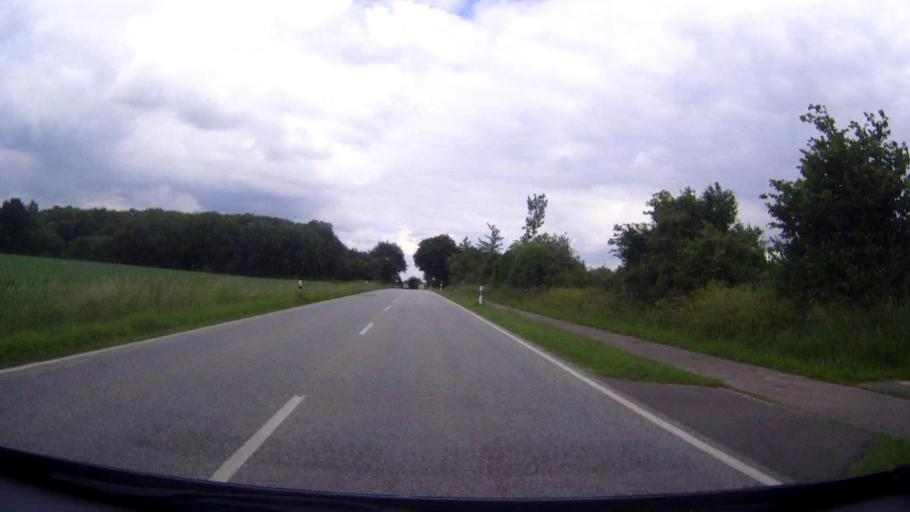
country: DE
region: Schleswig-Holstein
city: Hanerau-Hademarschen
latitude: 54.1253
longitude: 9.3977
